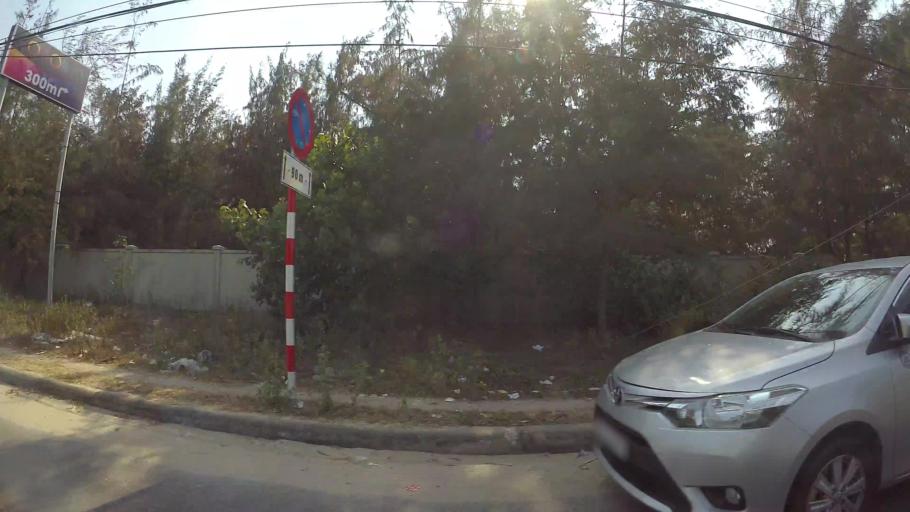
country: VN
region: Da Nang
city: Ngu Hanh Son
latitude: 15.9692
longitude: 108.2833
